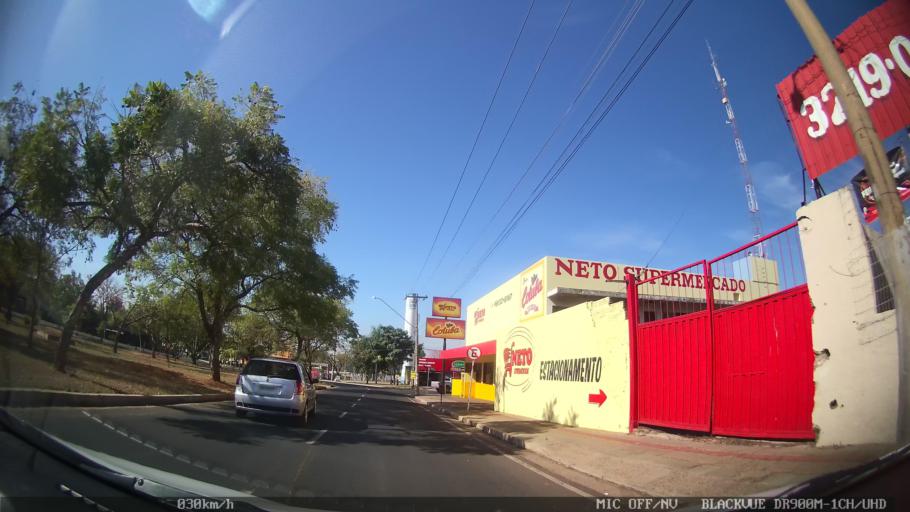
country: BR
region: Sao Paulo
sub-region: Sao Jose Do Rio Preto
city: Sao Jose do Rio Preto
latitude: -20.7857
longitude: -49.3921
